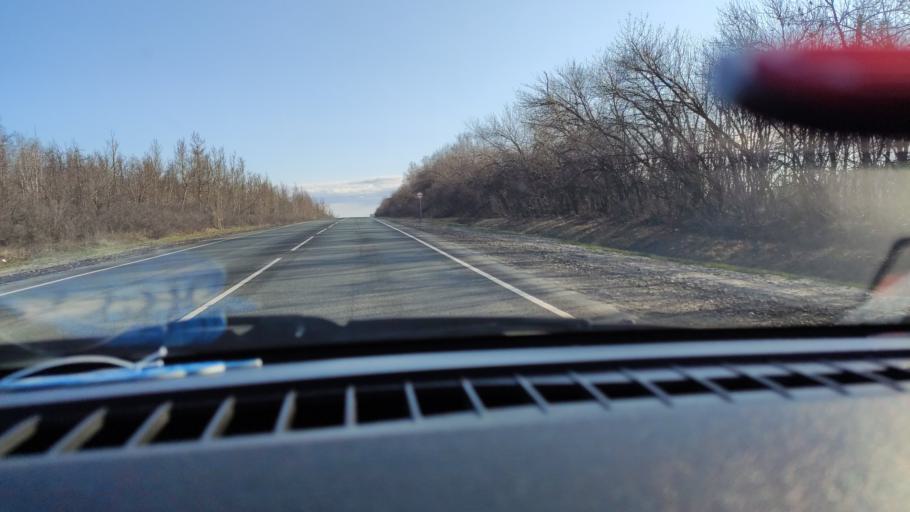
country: RU
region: Saratov
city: Dukhovnitskoye
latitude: 52.6215
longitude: 48.1737
